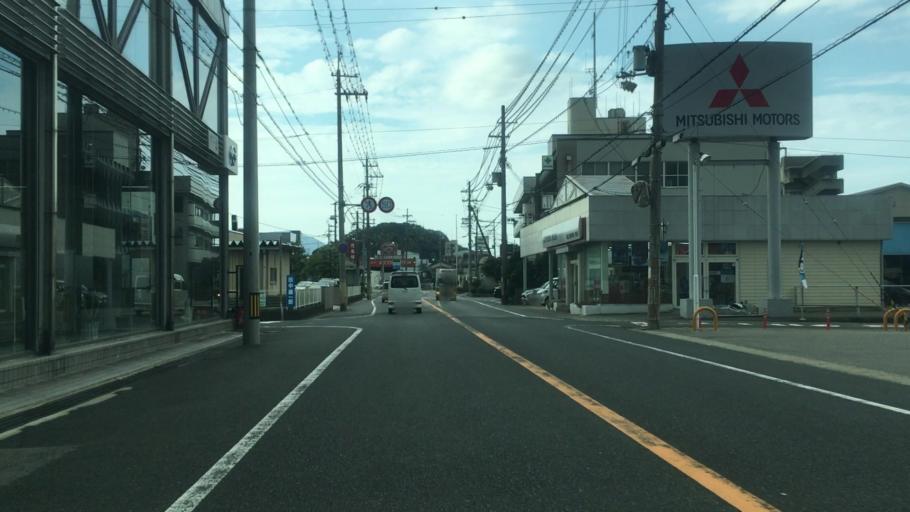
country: JP
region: Hyogo
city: Toyooka
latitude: 35.5299
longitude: 134.8200
